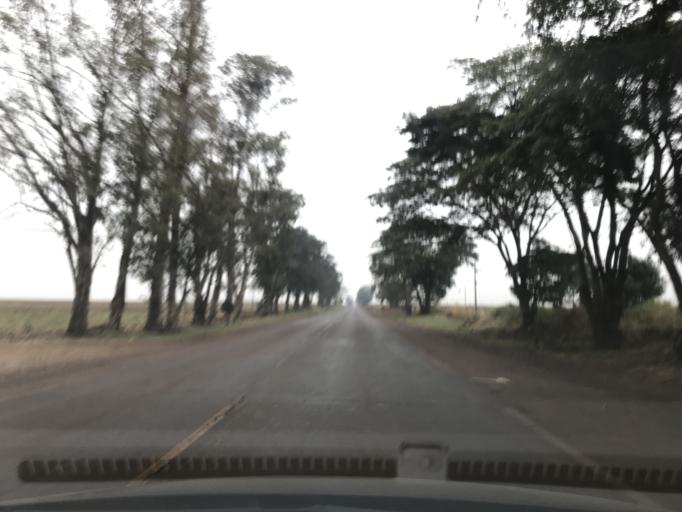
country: BR
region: Parana
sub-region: Palotina
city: Palotina
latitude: -24.3630
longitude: -53.8351
